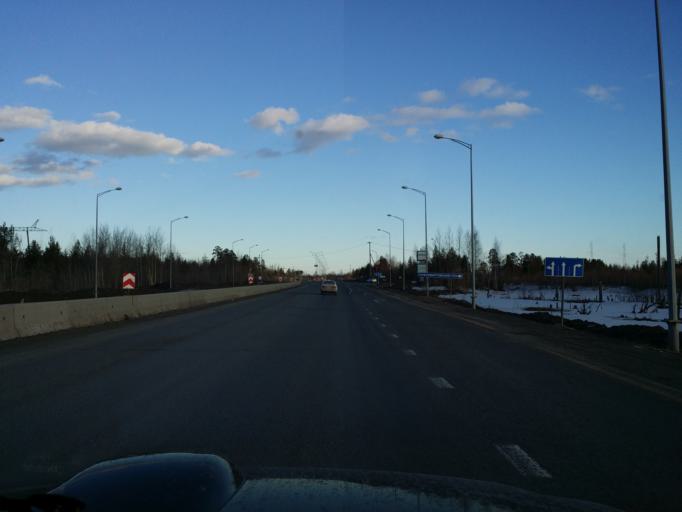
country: RU
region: Khanty-Mansiyskiy Avtonomnyy Okrug
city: Nizhnevartovsk
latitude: 60.9930
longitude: 76.4328
